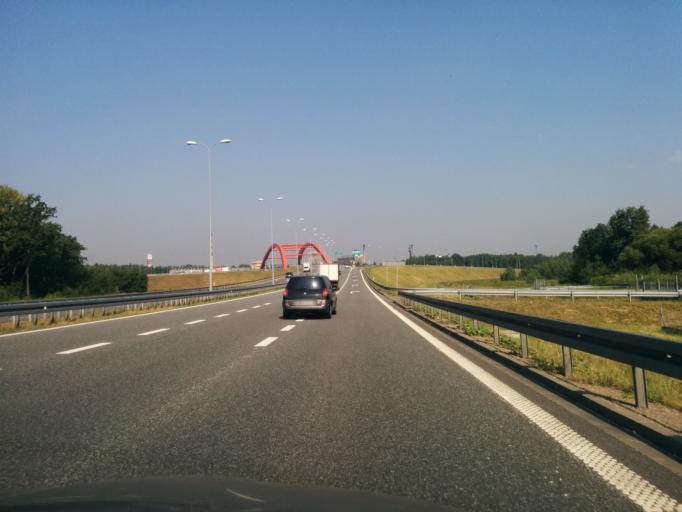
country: PL
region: Silesian Voivodeship
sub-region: Powiat gliwicki
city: Przyszowice
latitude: 50.2673
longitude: 18.7346
